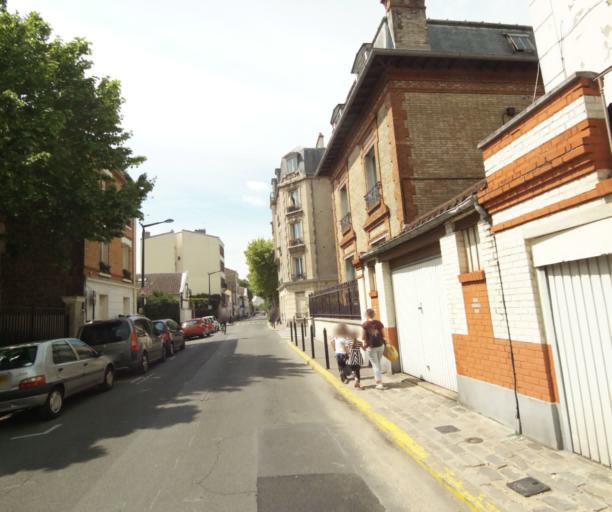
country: FR
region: Ile-de-France
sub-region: Departement des Hauts-de-Seine
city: Bois-Colombes
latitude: 48.9133
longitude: 2.2688
